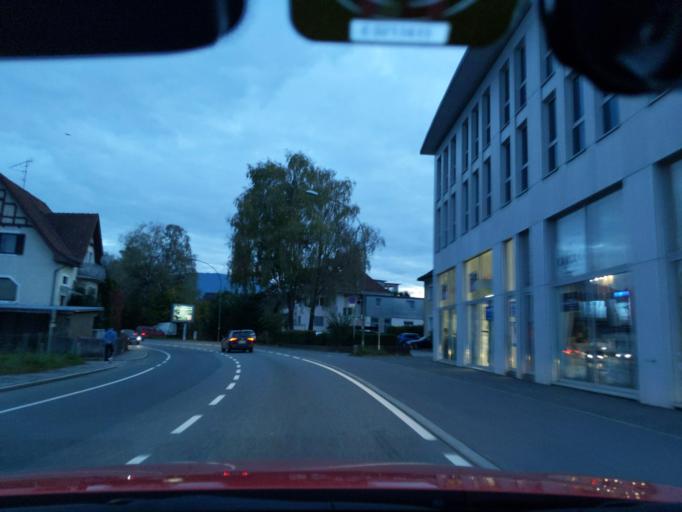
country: AT
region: Vorarlberg
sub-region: Politischer Bezirk Dornbirn
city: Lustenau
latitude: 47.4237
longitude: 9.6521
